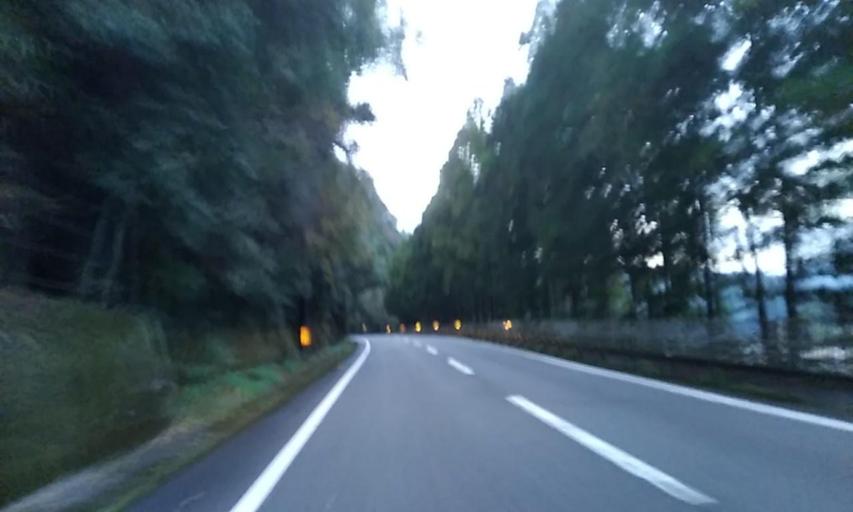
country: JP
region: Wakayama
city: Shingu
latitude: 33.7307
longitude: 135.9471
